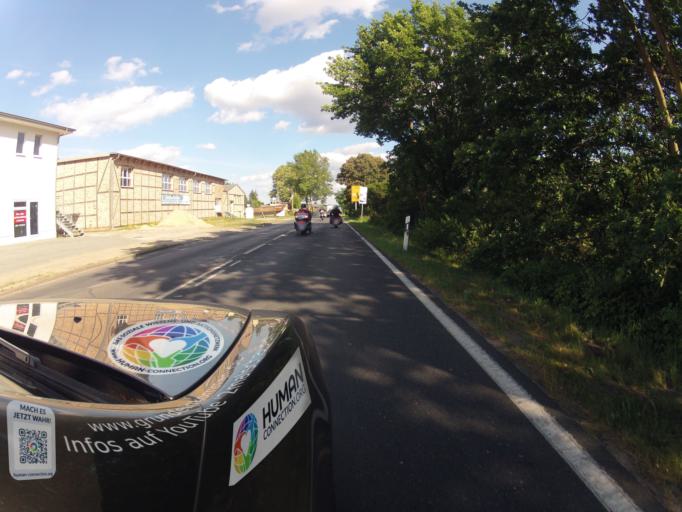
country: DE
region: Mecklenburg-Vorpommern
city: Seebad Bansin
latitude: 53.9652
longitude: 14.1282
